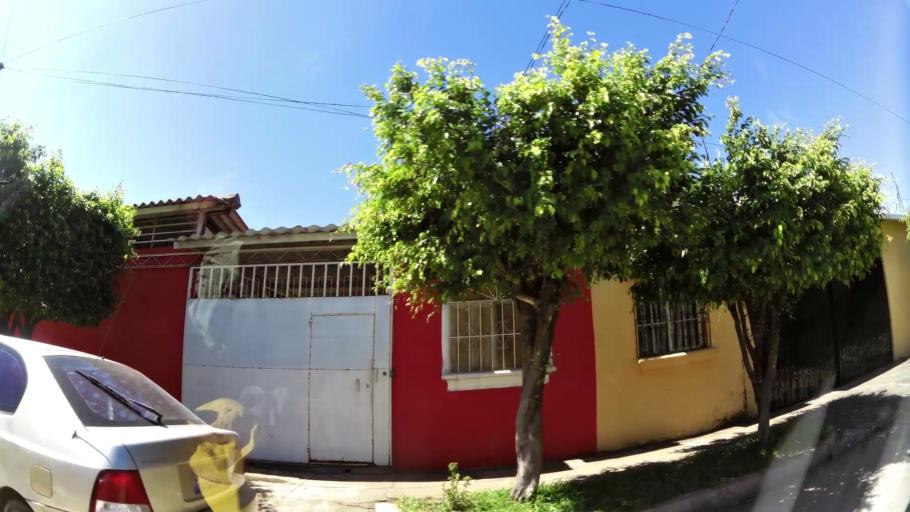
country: SV
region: La Libertad
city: San Juan Opico
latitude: 13.7970
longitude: -89.3574
